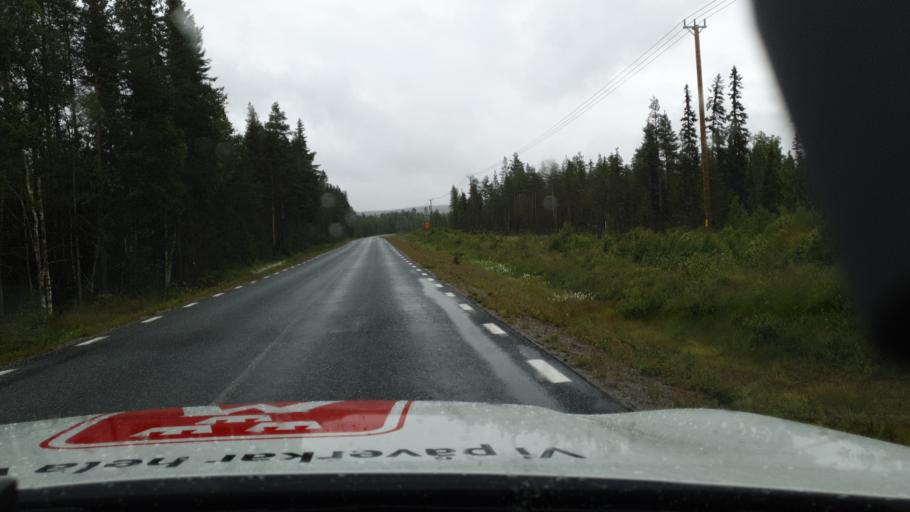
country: SE
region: Vaesterbotten
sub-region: Asele Kommun
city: Insjon
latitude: 64.2940
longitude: 17.6663
